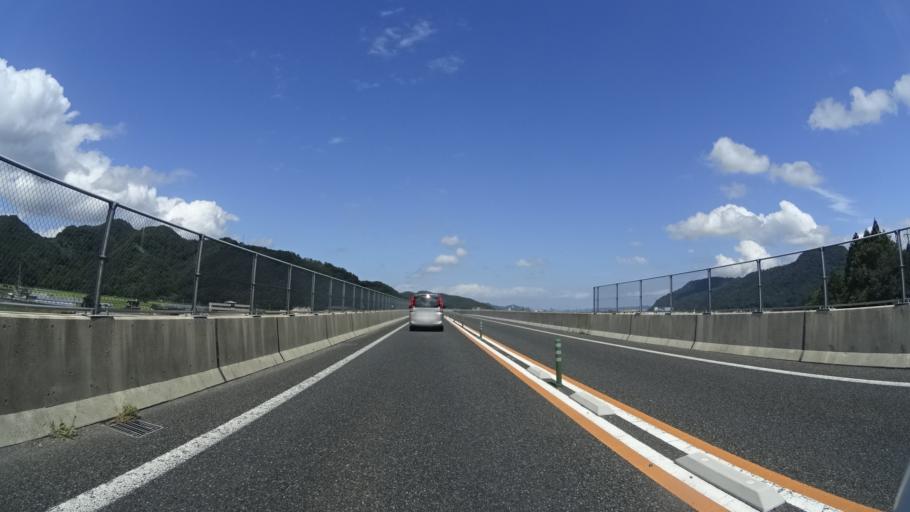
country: JP
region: Tottori
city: Tottori
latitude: 35.4161
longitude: 134.2064
